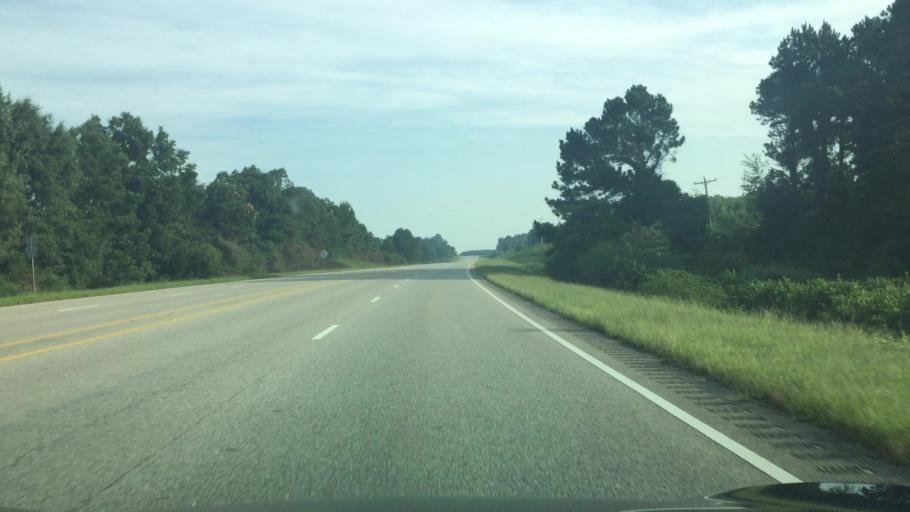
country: US
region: Alabama
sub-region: Covington County
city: Andalusia
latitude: 31.4250
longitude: -86.6116
